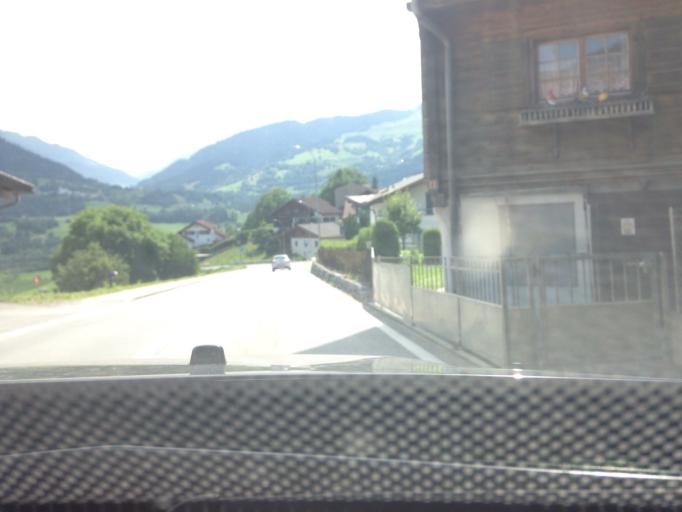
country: CH
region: Grisons
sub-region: Surselva District
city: Ilanz
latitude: 46.7875
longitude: 9.2254
